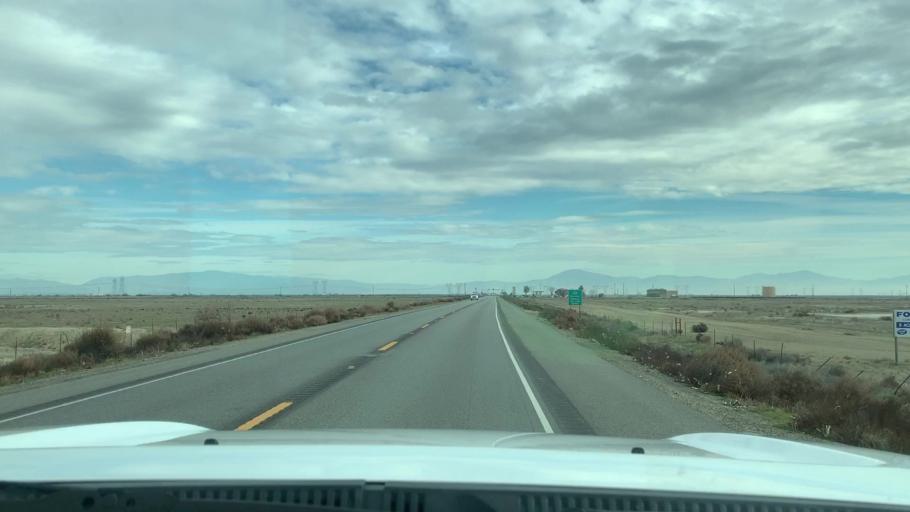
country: US
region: California
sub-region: Kern County
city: Rosedale
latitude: 35.2673
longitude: -119.2622
